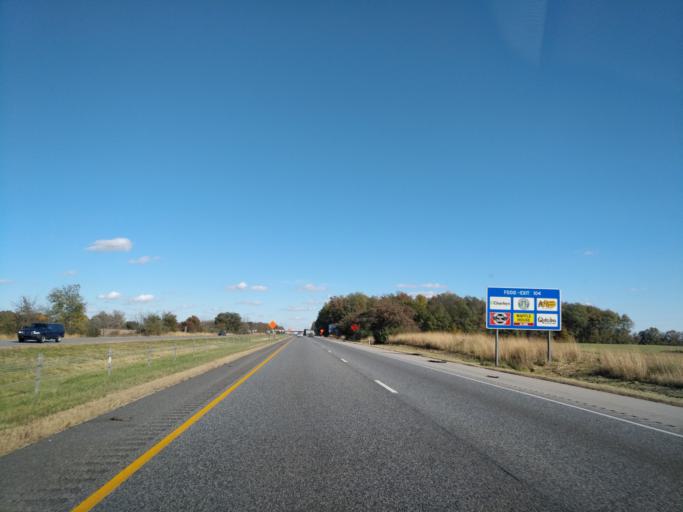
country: US
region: Indiana
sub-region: Hancock County
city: Greenfield
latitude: 39.8205
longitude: -85.8033
